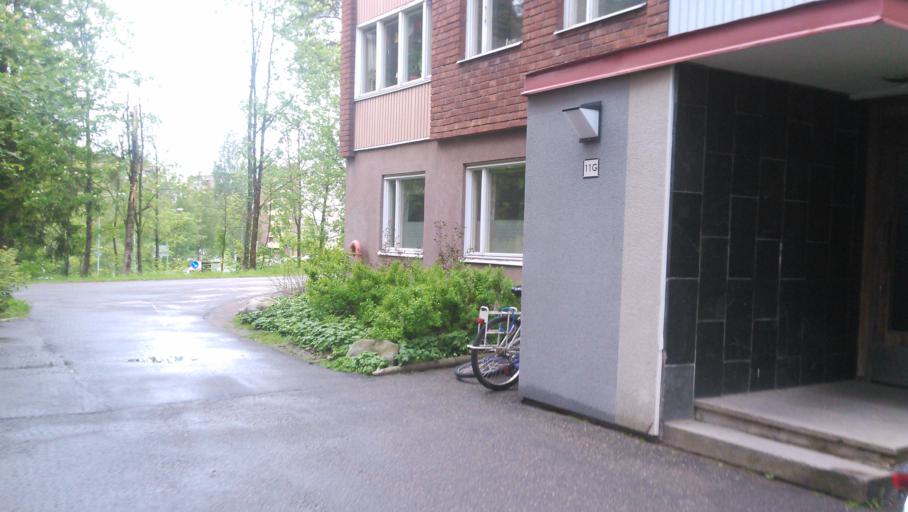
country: SE
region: Vaesterbotten
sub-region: Umea Kommun
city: Umea
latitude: 63.8129
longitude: 20.3068
